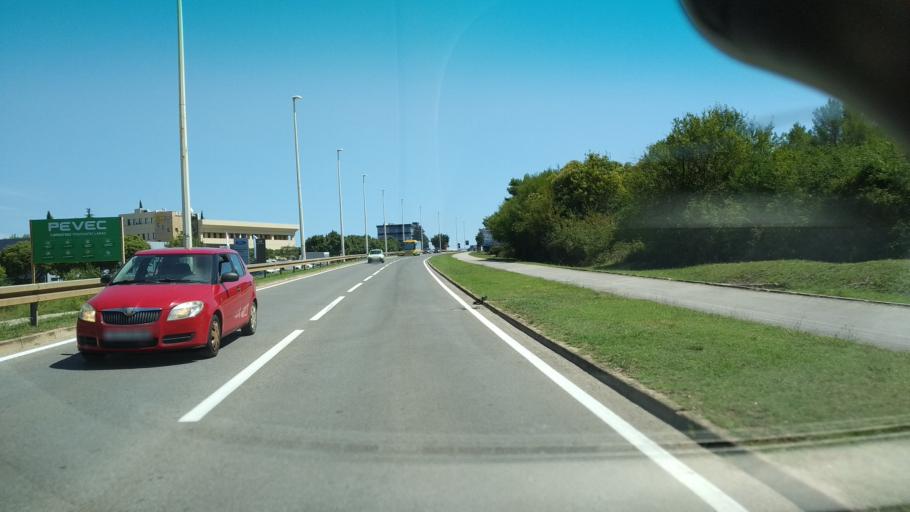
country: HR
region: Istarska
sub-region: Grad Pula
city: Pula
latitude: 44.8858
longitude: 13.8531
